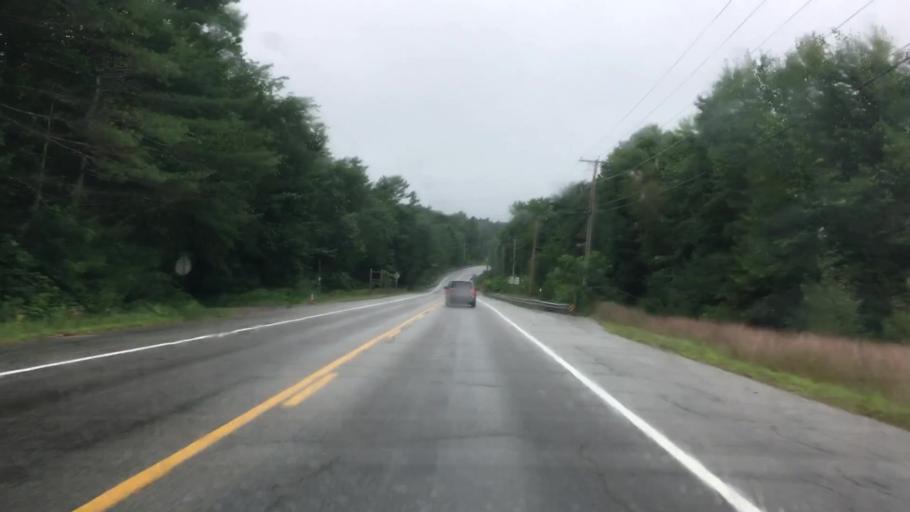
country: US
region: Maine
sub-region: Cumberland County
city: Raymond
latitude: 43.9577
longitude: -70.5632
